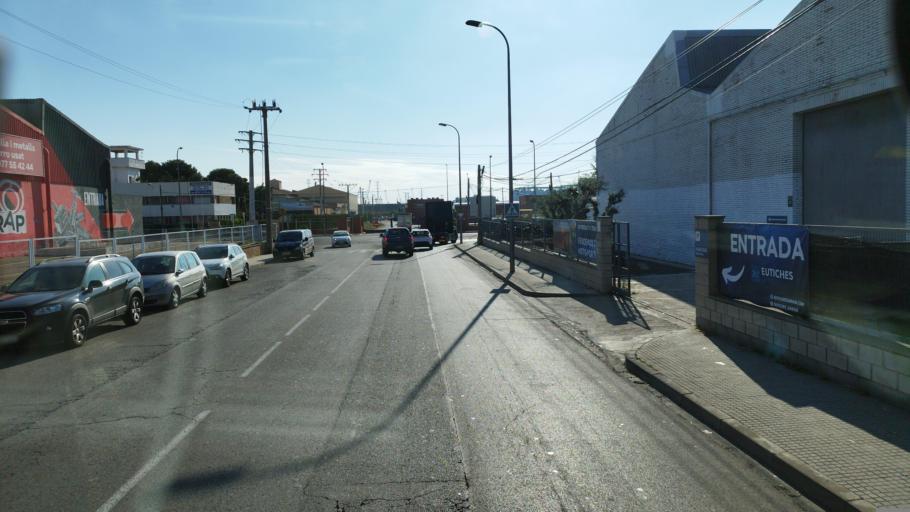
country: ES
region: Catalonia
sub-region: Provincia de Tarragona
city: Tarragona
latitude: 41.1144
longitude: 1.2328
